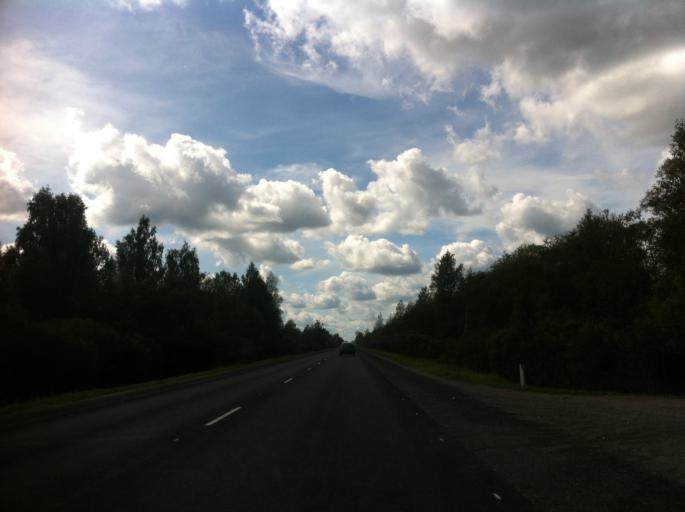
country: RU
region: Pskov
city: Izborsk
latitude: 57.7513
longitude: 28.0528
